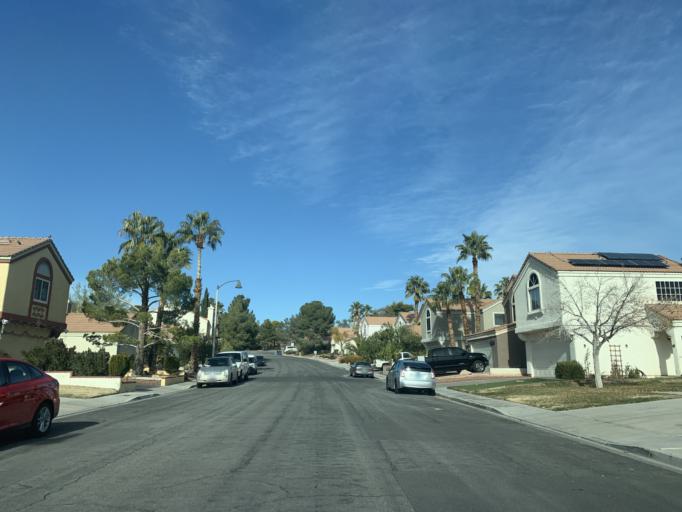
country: US
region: Nevada
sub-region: Clark County
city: Spring Valley
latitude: 36.1316
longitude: -115.2842
